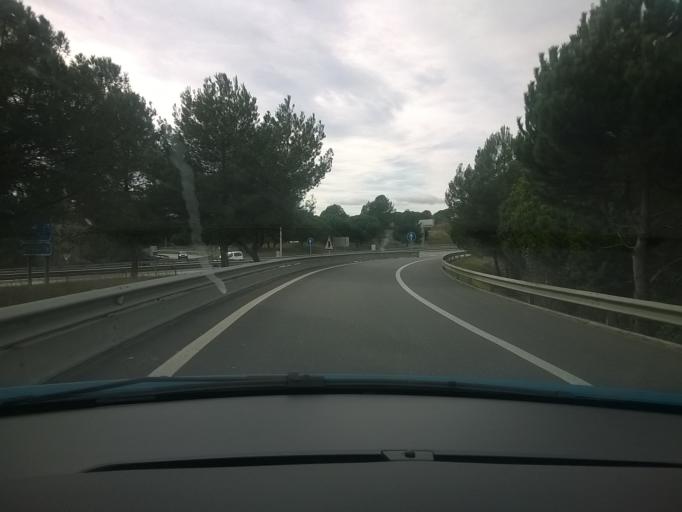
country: ES
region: Catalonia
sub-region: Provincia de Barcelona
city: Rubi
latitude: 41.4905
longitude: 2.0583
